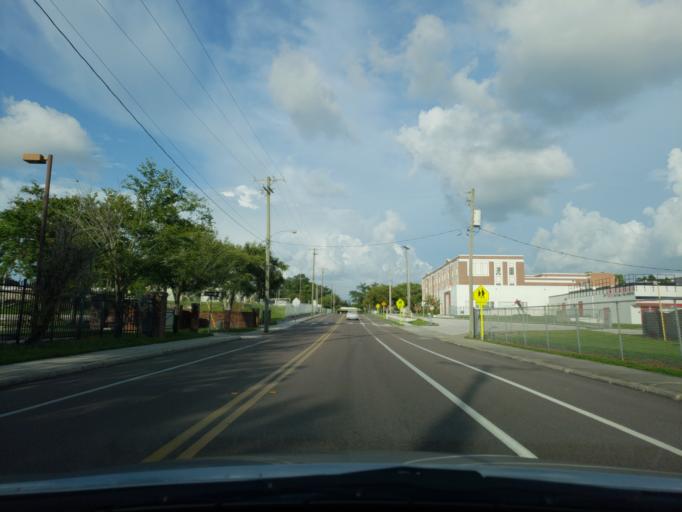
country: US
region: Florida
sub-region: Hillsborough County
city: Tampa
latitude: 27.9888
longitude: -82.4579
